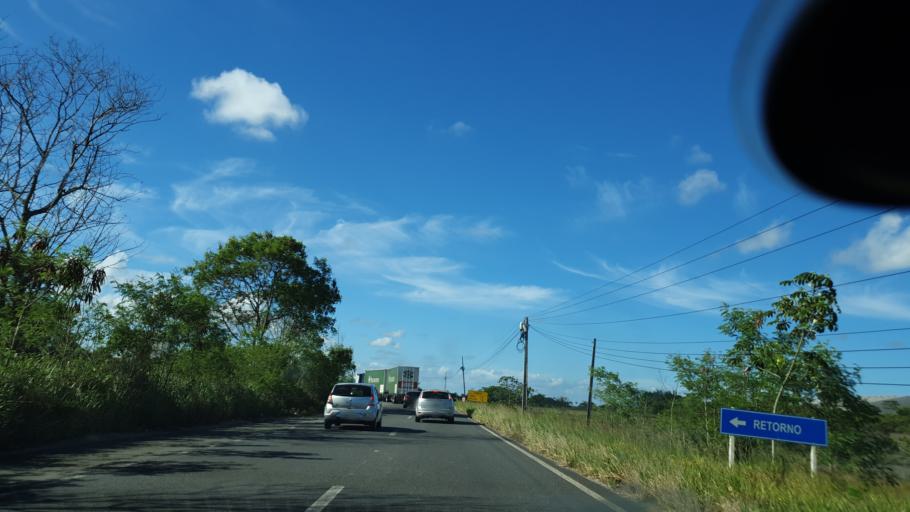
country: BR
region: Bahia
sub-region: Camacari
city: Camacari
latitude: -12.6687
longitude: -38.3000
